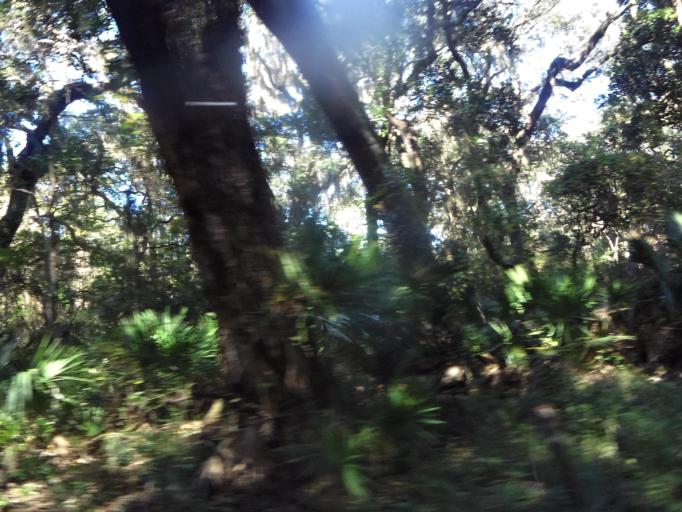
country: US
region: Florida
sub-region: Duval County
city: Atlantic Beach
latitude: 30.4351
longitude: -81.4309
